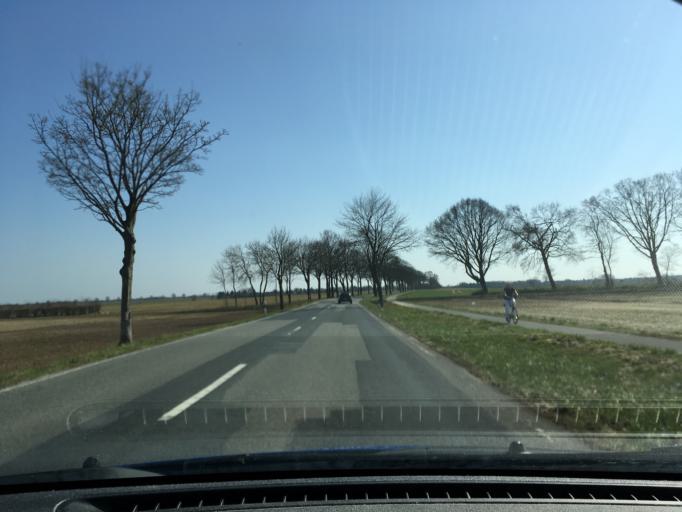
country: DE
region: Lower Saxony
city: Wriedel
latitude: 53.0457
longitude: 10.2950
